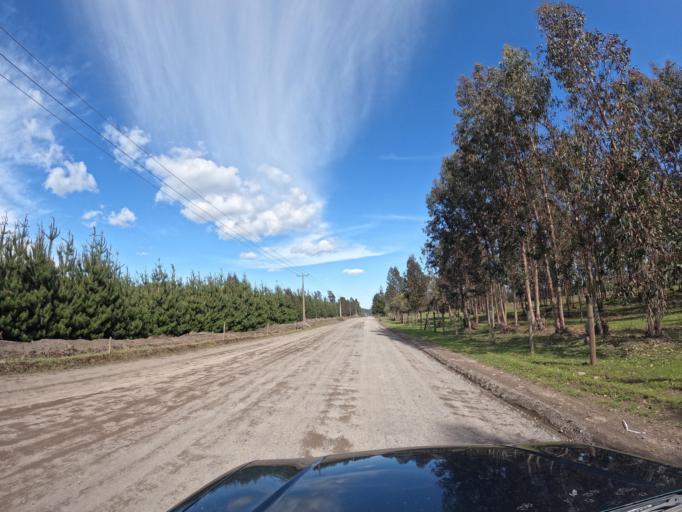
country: CL
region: Biobio
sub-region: Provincia de Concepcion
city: Chiguayante
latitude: -37.0649
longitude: -72.9480
